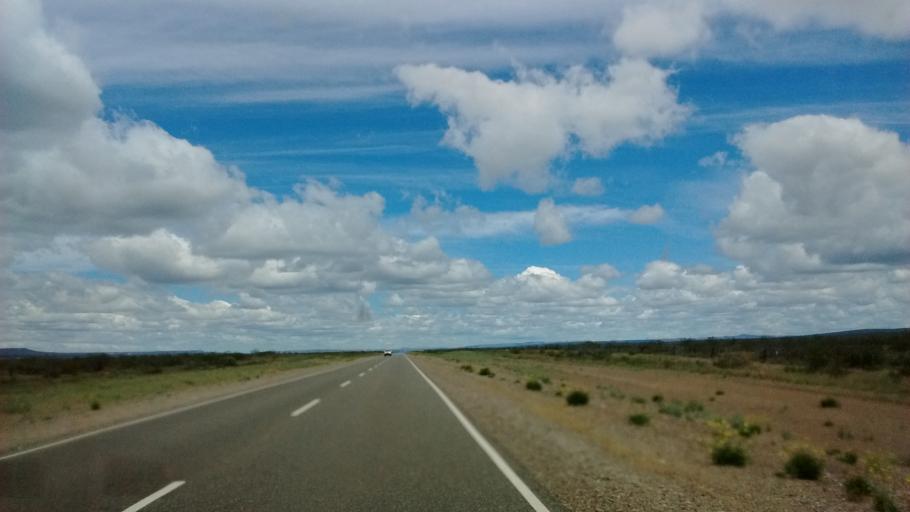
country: AR
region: Neuquen
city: Piedra del Aguila
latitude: -39.8053
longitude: -69.7039
